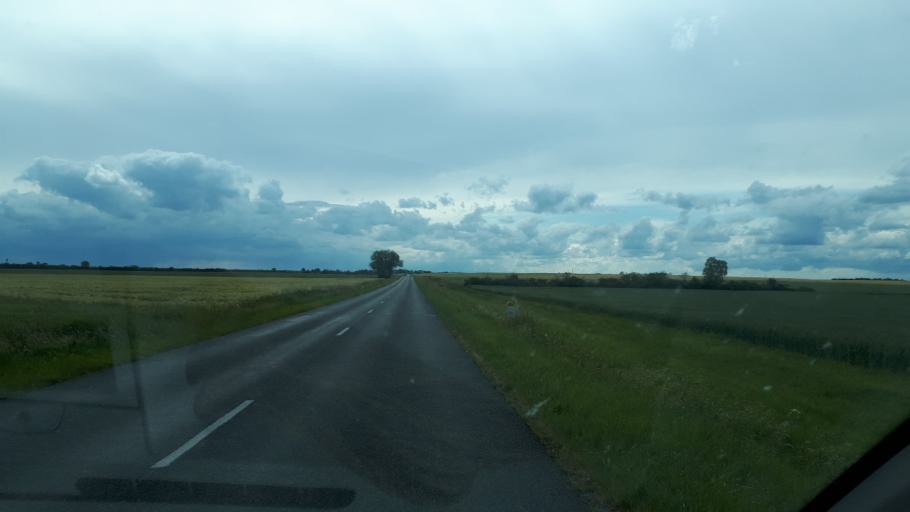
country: FR
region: Centre
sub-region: Departement du Cher
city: Marmagne
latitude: 47.0813
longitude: 2.2285
